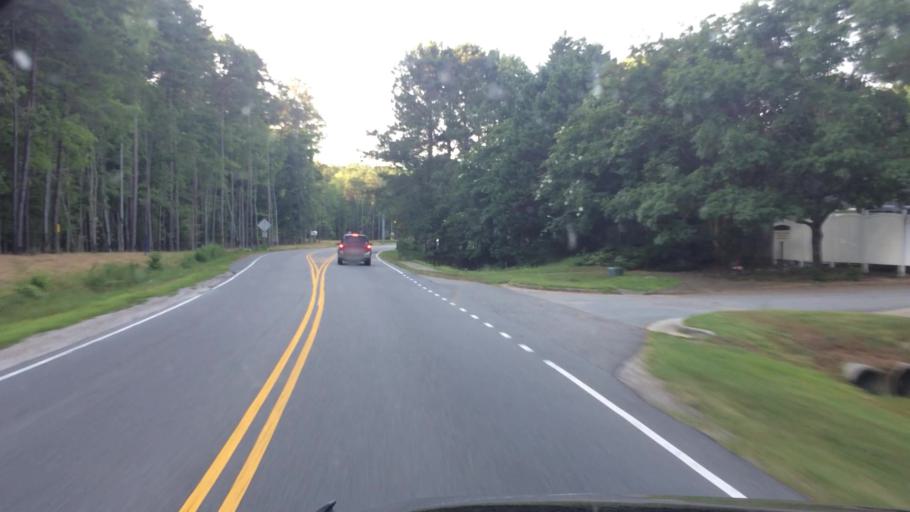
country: US
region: Virginia
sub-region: James City County
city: Williamsburg
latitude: 37.3147
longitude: -76.7304
